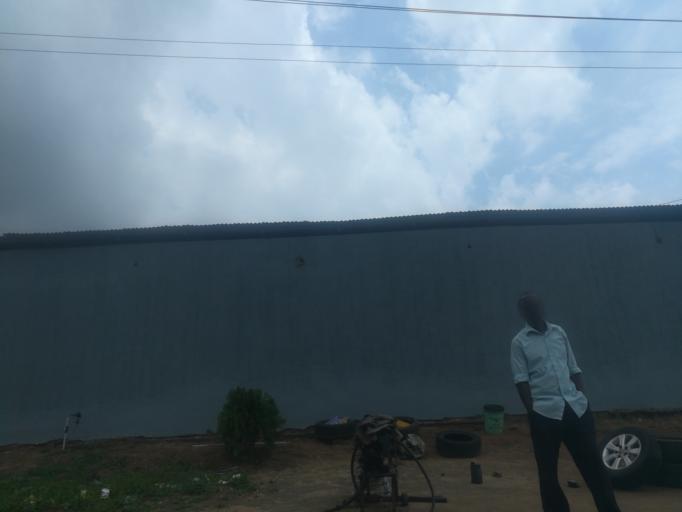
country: NG
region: Lagos
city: Ojota
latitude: 6.5884
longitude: 3.3874
